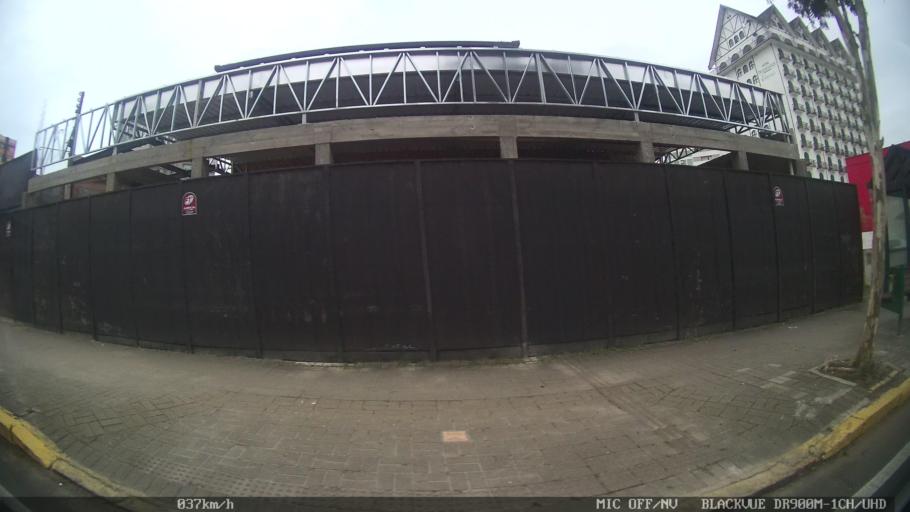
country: BR
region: Santa Catarina
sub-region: Joinville
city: Joinville
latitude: -26.3043
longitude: -48.8512
